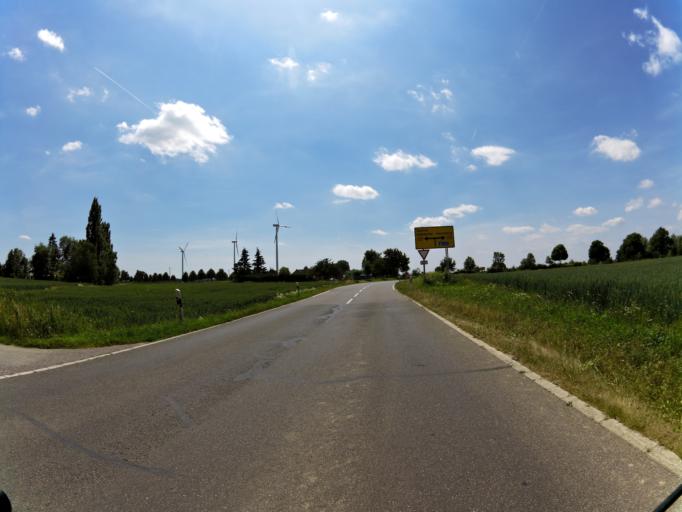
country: DE
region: North Rhine-Westphalia
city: Geilenkirchen
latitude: 51.0147
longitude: 6.1179
